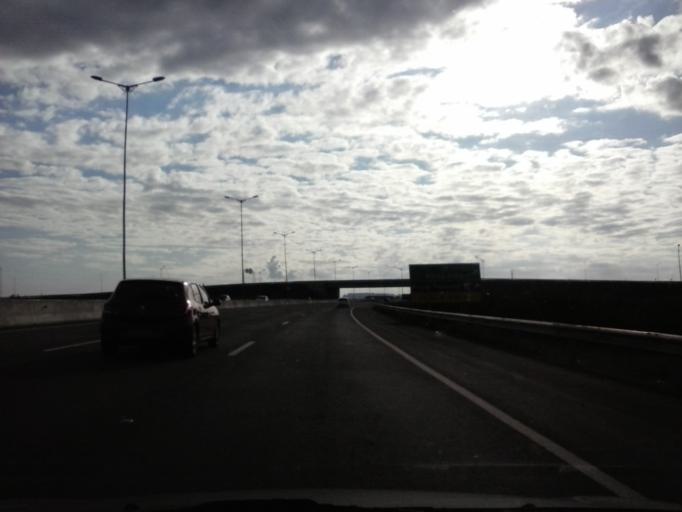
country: BR
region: Rio Grande do Sul
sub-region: Canoas
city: Canoas
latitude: -29.9245
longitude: -51.2266
